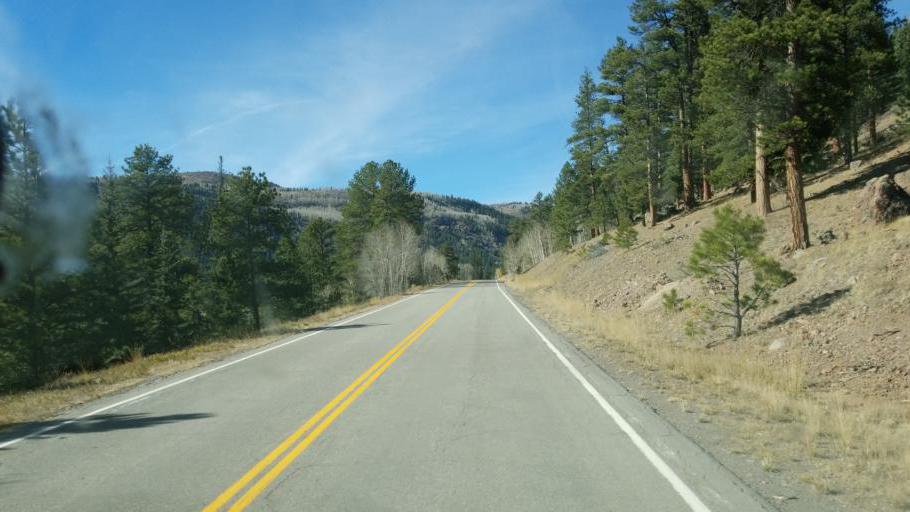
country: US
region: Colorado
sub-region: Conejos County
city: Conejos
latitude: 37.0798
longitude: -106.2951
